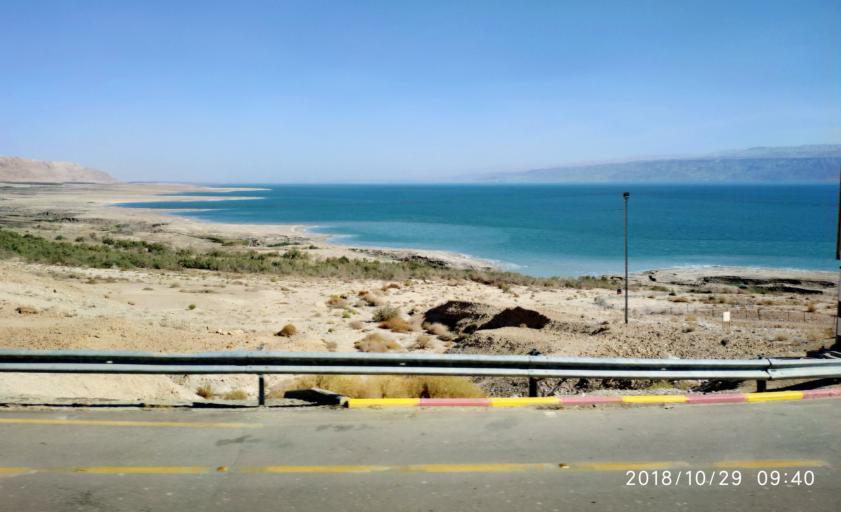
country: PS
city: `Arab ar Rashaydah
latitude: 31.5816
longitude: 35.4067
